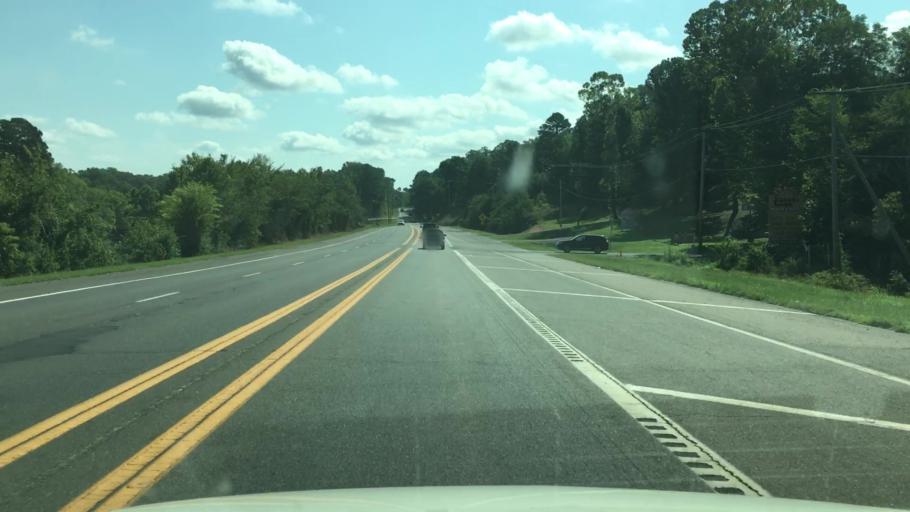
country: US
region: Arkansas
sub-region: Garland County
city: Piney
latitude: 34.5082
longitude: -93.1797
